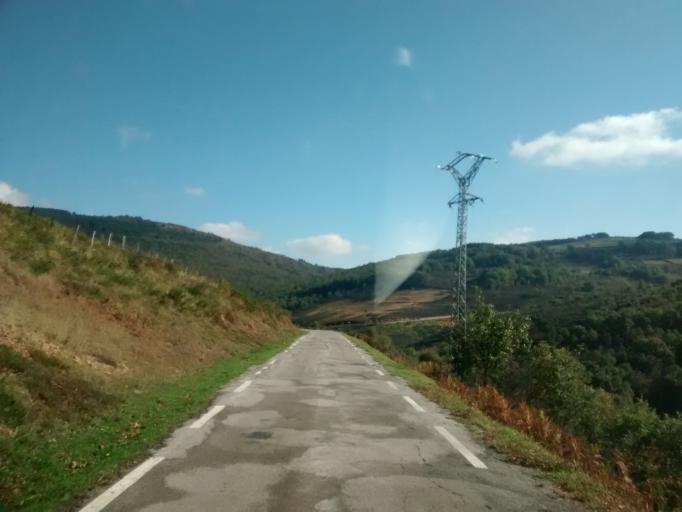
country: ES
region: Castille and Leon
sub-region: Provincia de Burgos
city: Arija
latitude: 42.9293
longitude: -4.0205
